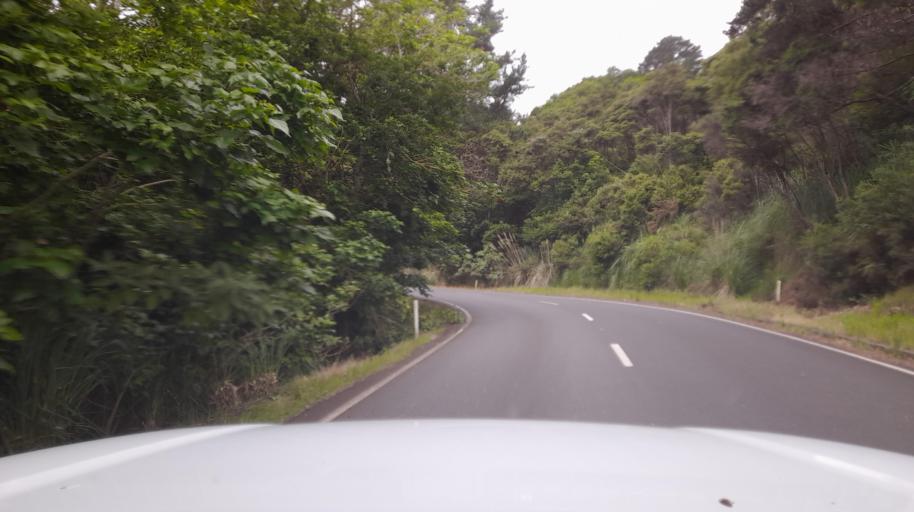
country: NZ
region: Northland
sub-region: Far North District
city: Kaitaia
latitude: -35.3598
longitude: 173.4555
